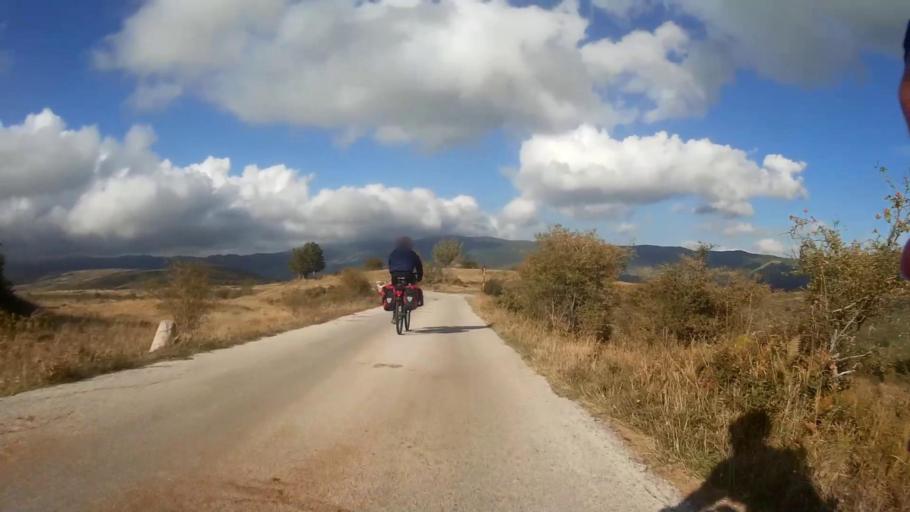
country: IT
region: Basilicate
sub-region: Provincia di Potenza
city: Viggianello
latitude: 39.9578
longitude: 16.1431
